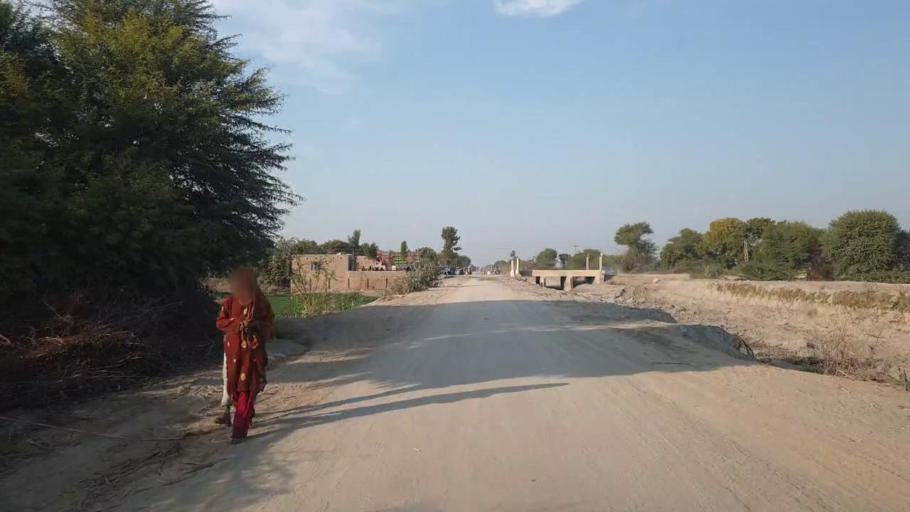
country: PK
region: Sindh
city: Shahpur Chakar
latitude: 26.1567
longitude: 68.6407
